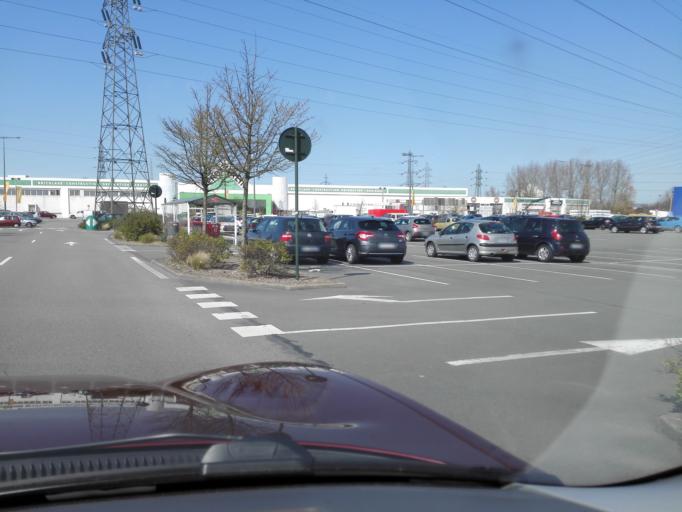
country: FR
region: Nord-Pas-de-Calais
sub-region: Departement du Nord
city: Grande-Synthe
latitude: 51.0061
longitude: 2.2809
